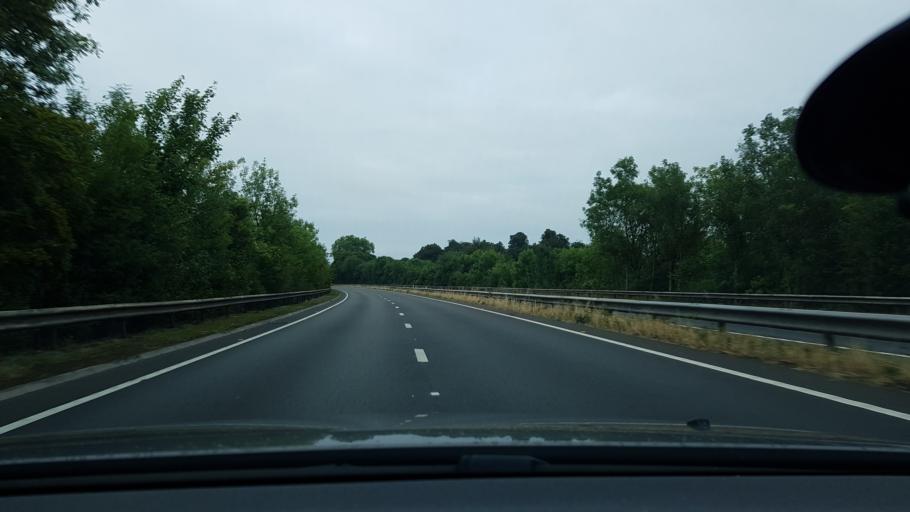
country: GB
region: England
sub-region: Hampshire
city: Overton
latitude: 51.2307
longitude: -1.3487
